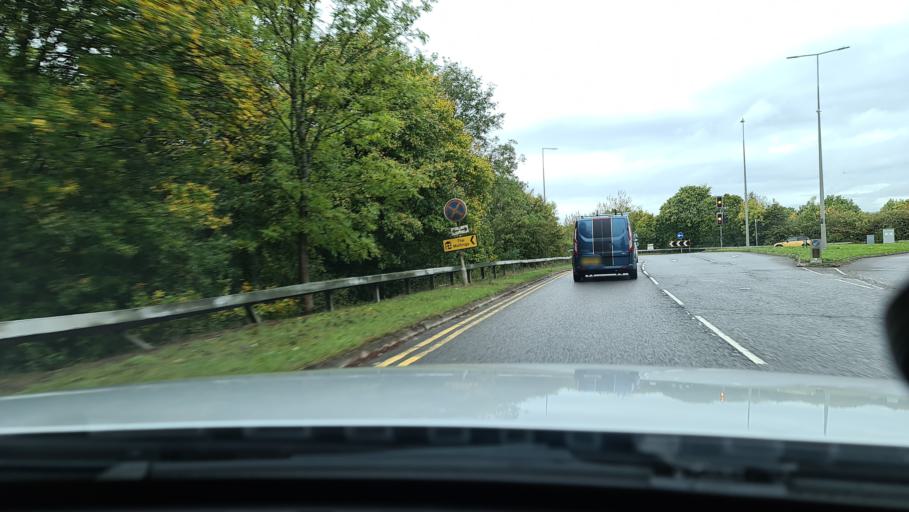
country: GB
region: England
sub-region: Buckinghamshire
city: Bletchley
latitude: 52.0103
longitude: -0.7391
